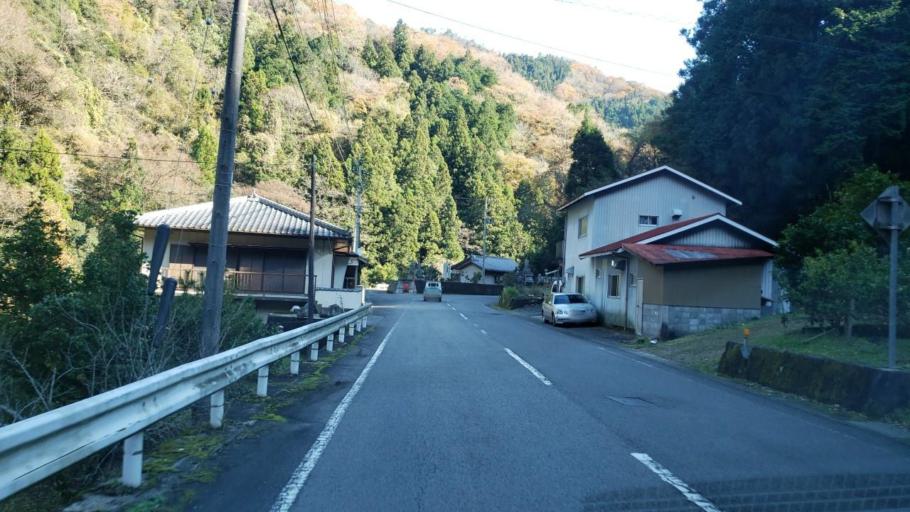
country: JP
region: Tokushima
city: Wakimachi
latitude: 34.0075
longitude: 134.0325
